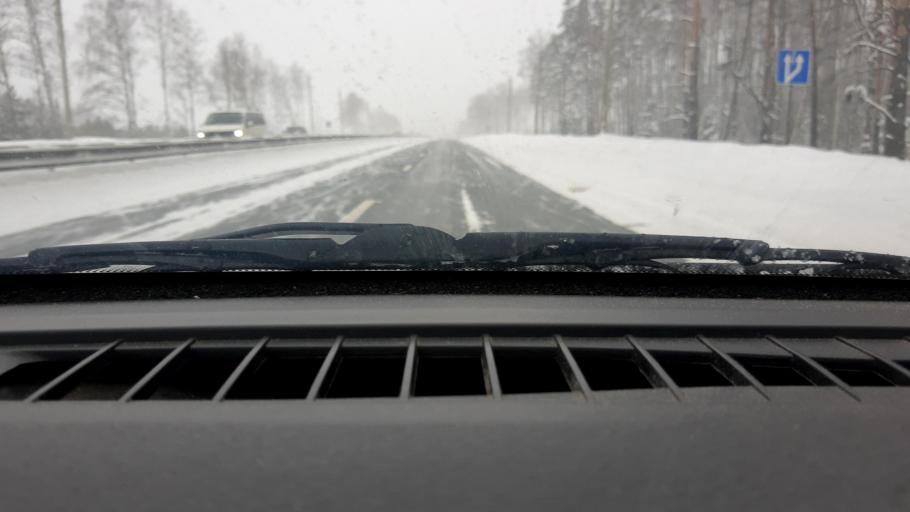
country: RU
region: Vladimir
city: Melekhovo
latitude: 56.2132
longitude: 41.3452
